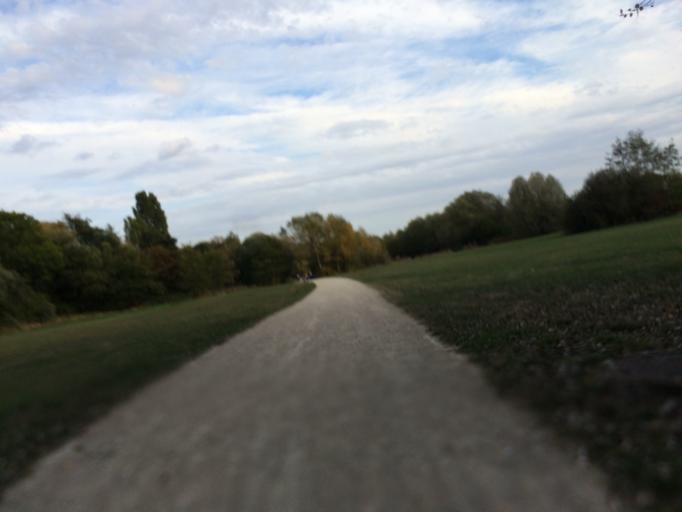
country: FR
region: Ile-de-France
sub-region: Departement de l'Essonne
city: Linas
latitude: 48.6367
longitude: 2.2564
